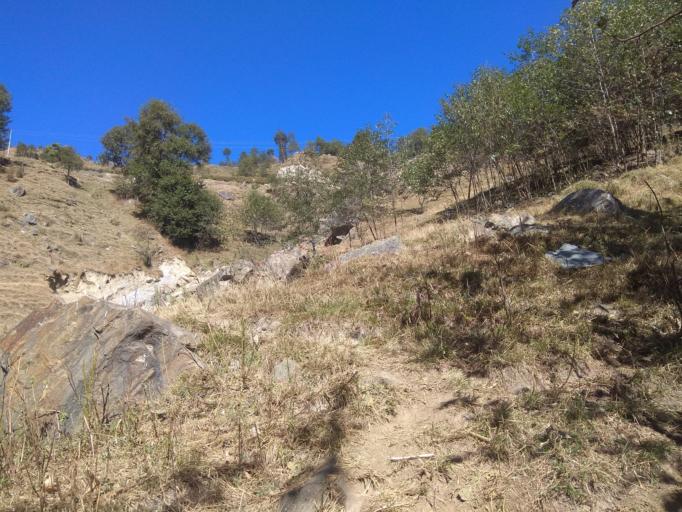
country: NP
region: Far Western
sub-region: Seti Zone
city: Achham
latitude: 29.2558
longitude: 81.6313
